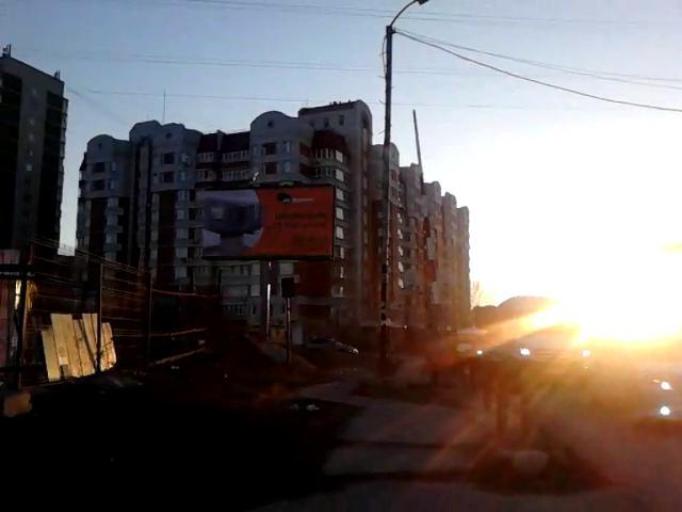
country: RU
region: Sverdlovsk
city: Yekaterinburg
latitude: 56.8430
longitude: 60.6922
